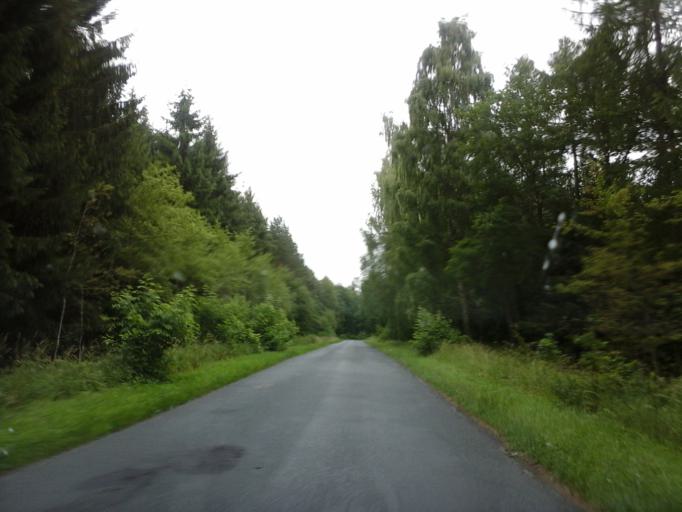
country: PL
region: West Pomeranian Voivodeship
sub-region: Powiat stargardzki
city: Dolice
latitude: 53.2325
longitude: 15.2589
